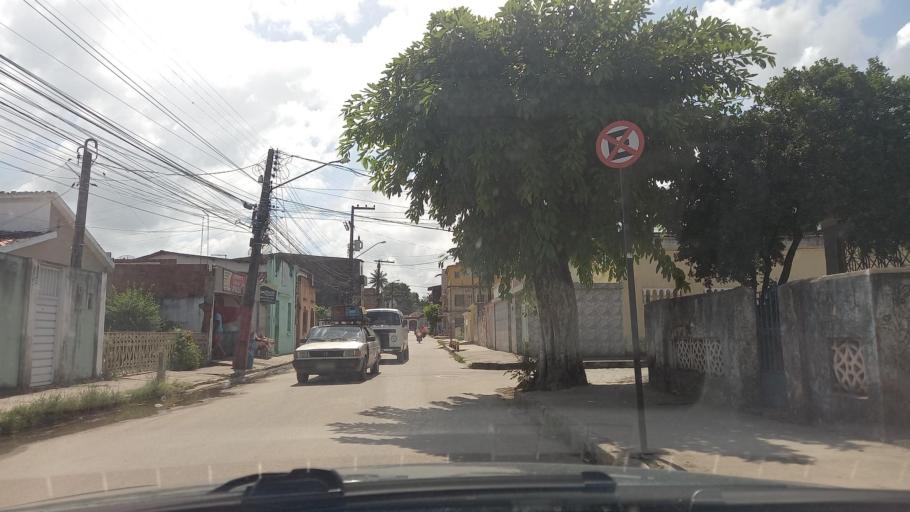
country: BR
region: Pernambuco
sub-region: Goiana
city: Goiana
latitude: -7.5614
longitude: -35.0022
